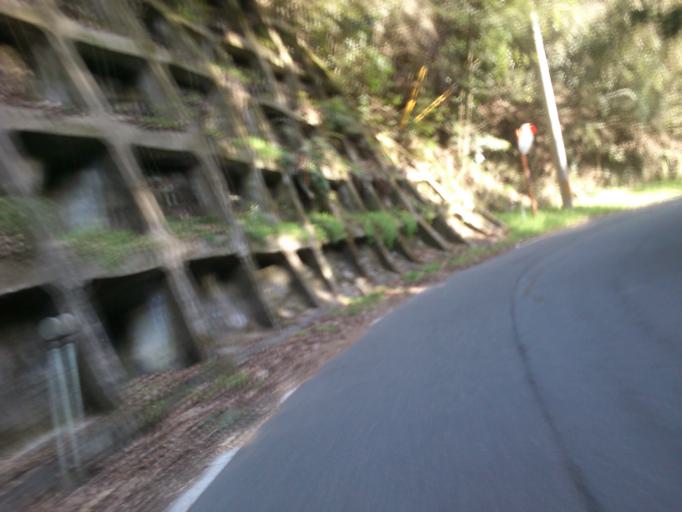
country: JP
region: Kyoto
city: Yawata
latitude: 34.9154
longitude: 135.6630
